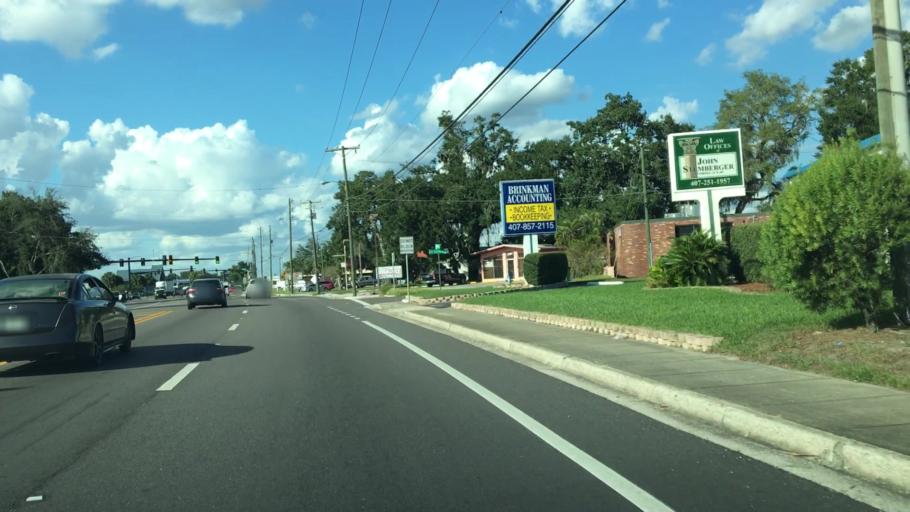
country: US
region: Florida
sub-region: Orange County
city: Edgewood
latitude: 28.4925
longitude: -81.3739
